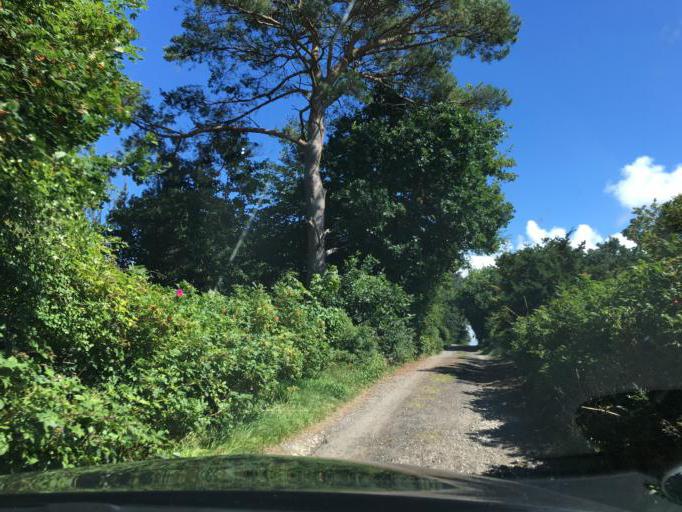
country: DK
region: Capital Region
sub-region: Gribskov Kommune
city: Helsinge
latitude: 56.0953
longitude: 12.1642
